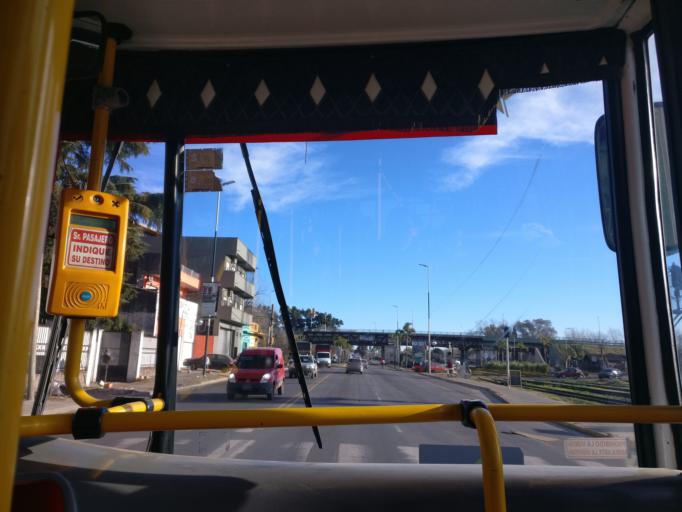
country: AR
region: Buenos Aires
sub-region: Partido de Ezeiza
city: Ezeiza
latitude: -34.8606
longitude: -58.5307
